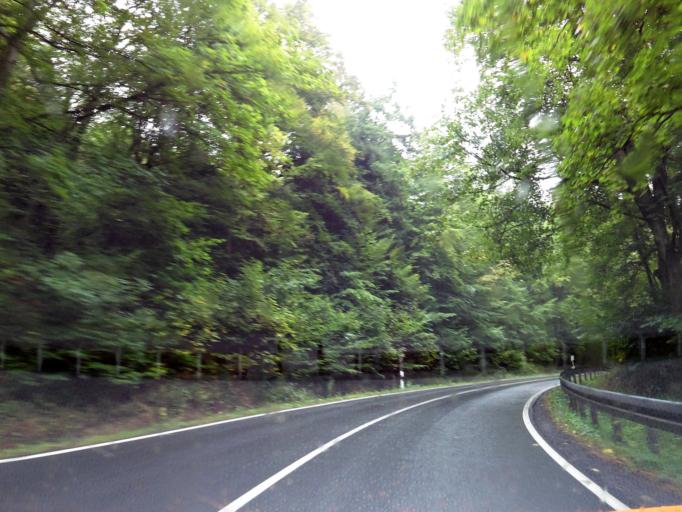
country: DE
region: Saxony-Anhalt
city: Harzgerode
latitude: 51.6601
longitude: 11.1244
